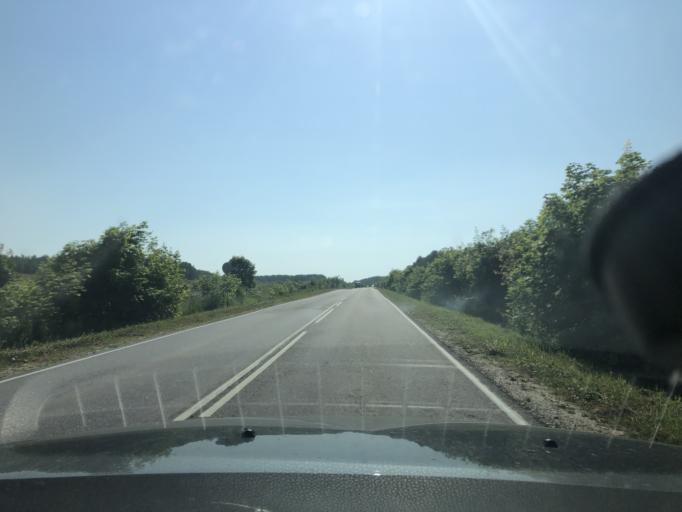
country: RU
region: Tula
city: Dubna
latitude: 54.1426
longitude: 37.0013
